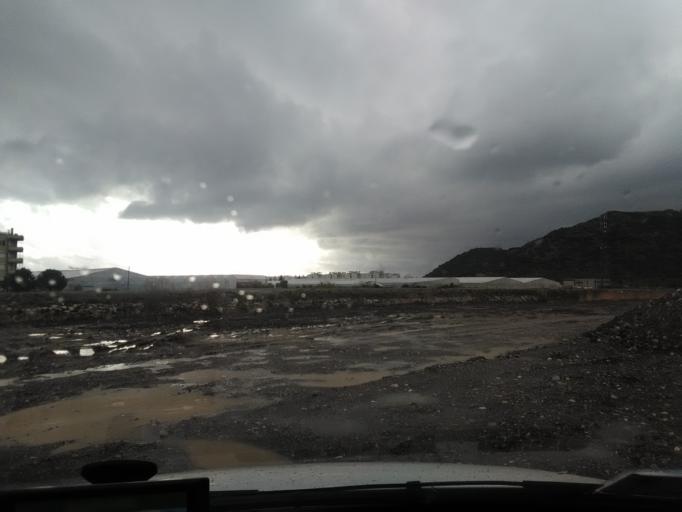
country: TR
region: Antalya
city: Gazipasa
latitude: 36.2618
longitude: 32.2970
